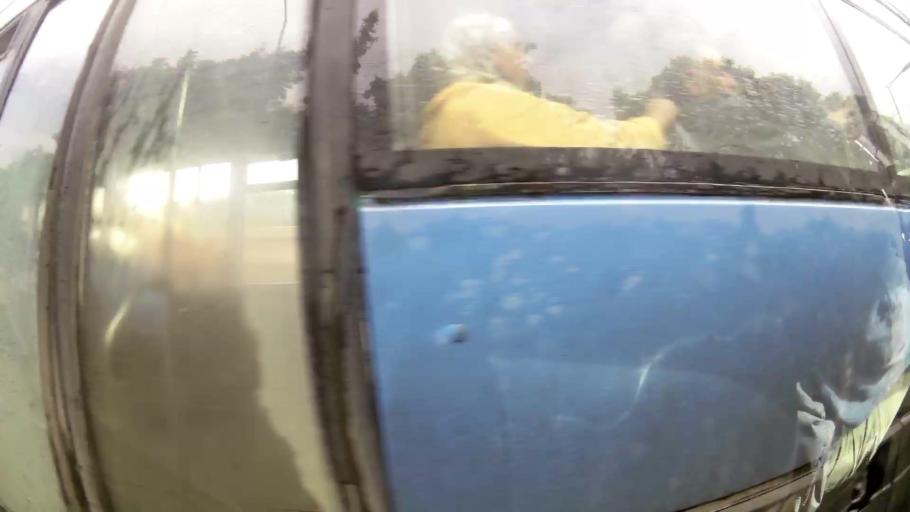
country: MA
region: Grand Casablanca
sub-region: Casablanca
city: Casablanca
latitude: 33.5667
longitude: -7.6371
